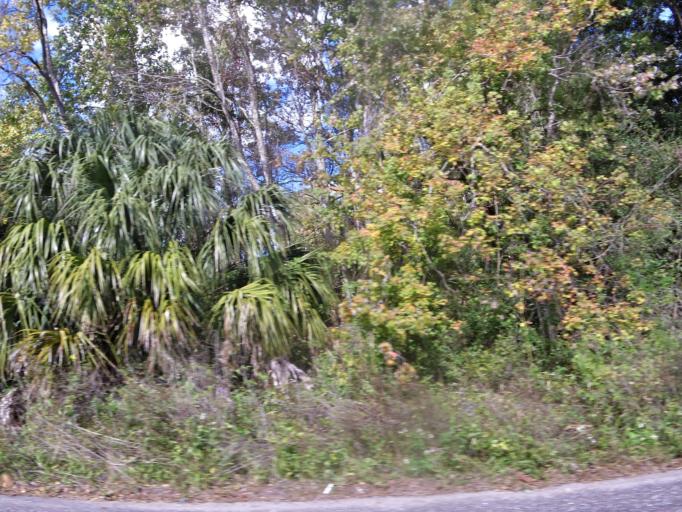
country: US
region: Florida
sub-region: Duval County
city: Jacksonville
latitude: 30.4101
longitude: -81.6416
